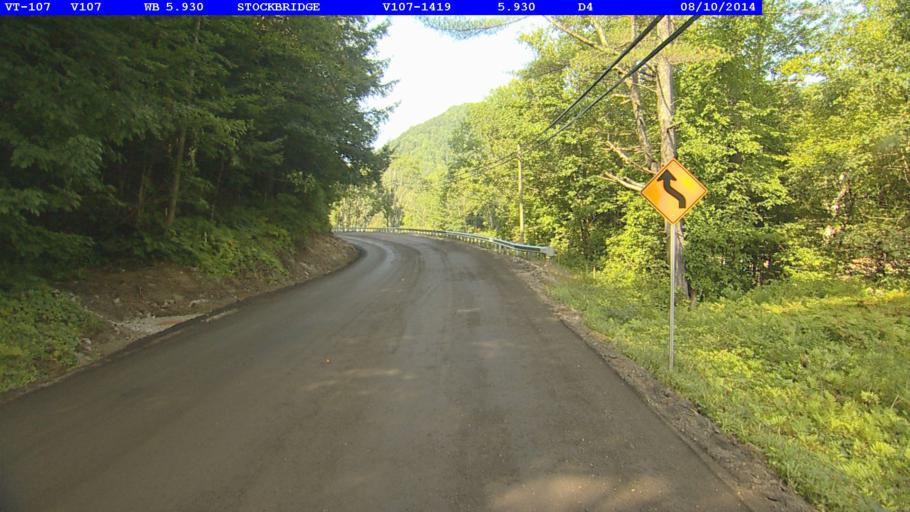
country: US
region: Vermont
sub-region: Orange County
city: Randolph
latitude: 43.7922
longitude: -72.6764
